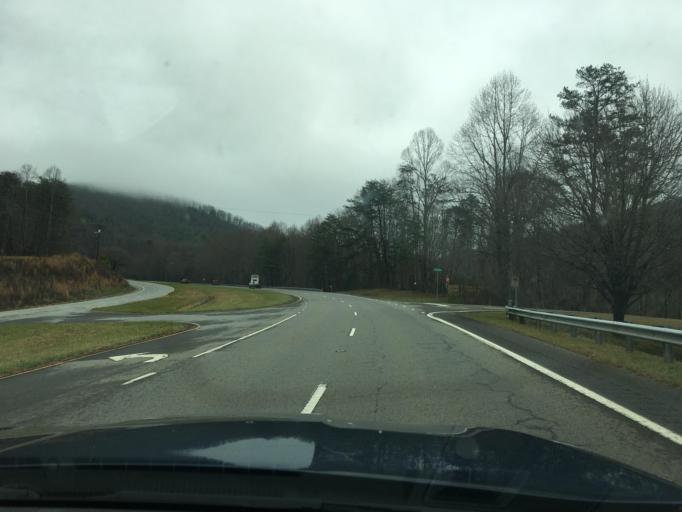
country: US
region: Georgia
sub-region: Fannin County
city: McCaysville
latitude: 35.0132
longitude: -84.2959
